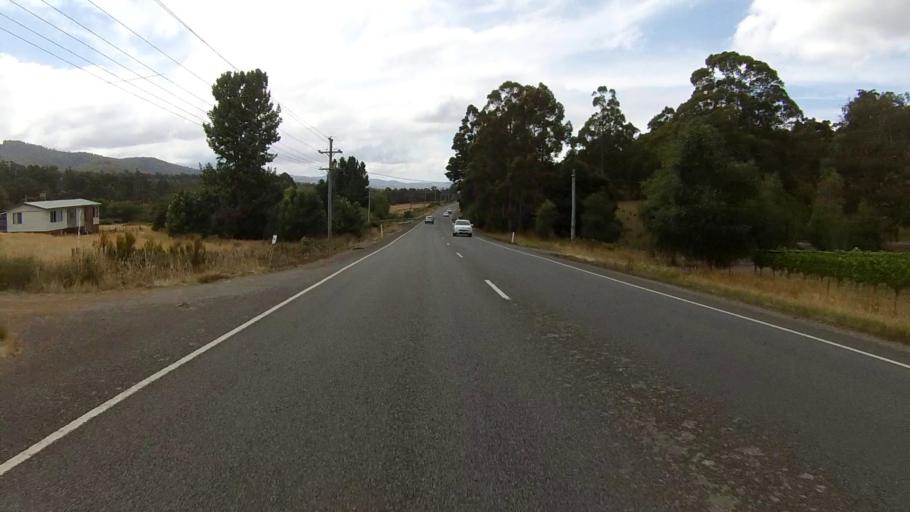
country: AU
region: Tasmania
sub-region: Kingborough
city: Kettering
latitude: -43.0872
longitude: 147.2513
